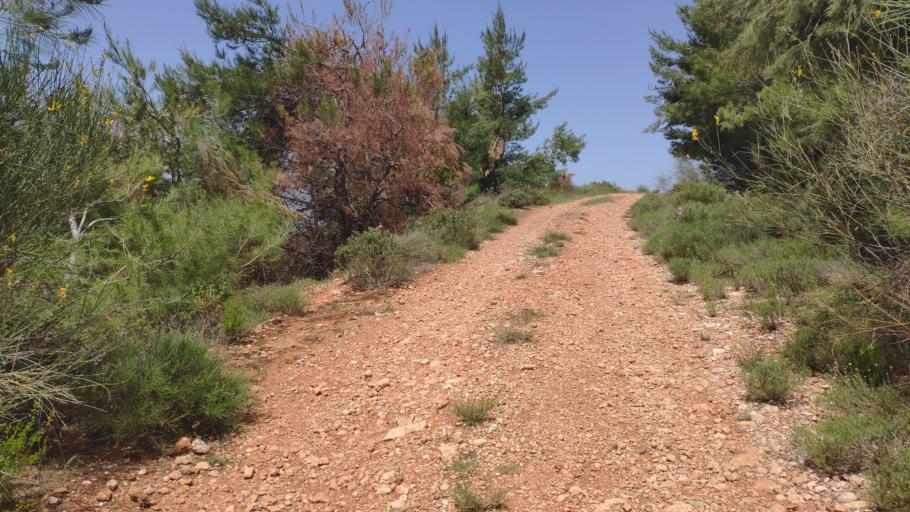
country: GR
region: Attica
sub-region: Nomarchia Anatolikis Attikis
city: Kalamos
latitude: 38.2852
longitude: 23.8511
